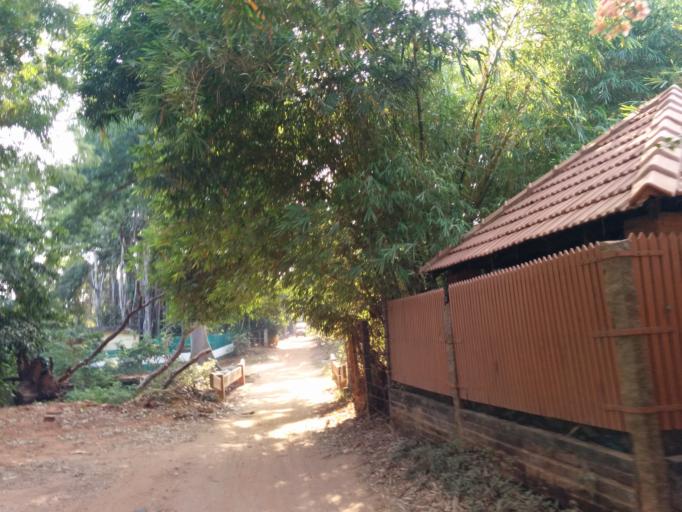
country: IN
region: Tamil Nadu
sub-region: Villupuram
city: Auroville
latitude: 11.9872
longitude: 79.8327
